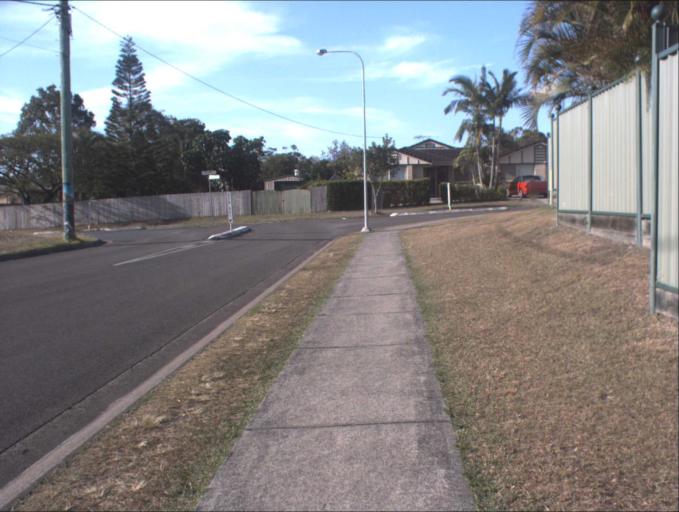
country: AU
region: Queensland
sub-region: Logan
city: Slacks Creek
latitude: -27.6629
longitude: 153.1809
